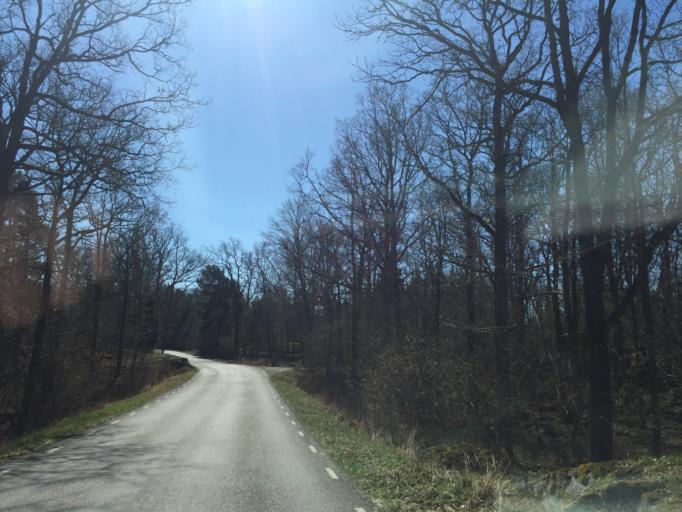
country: SE
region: Kalmar
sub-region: Oskarshamns Kommun
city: Oskarshamn
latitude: 57.2389
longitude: 16.4774
